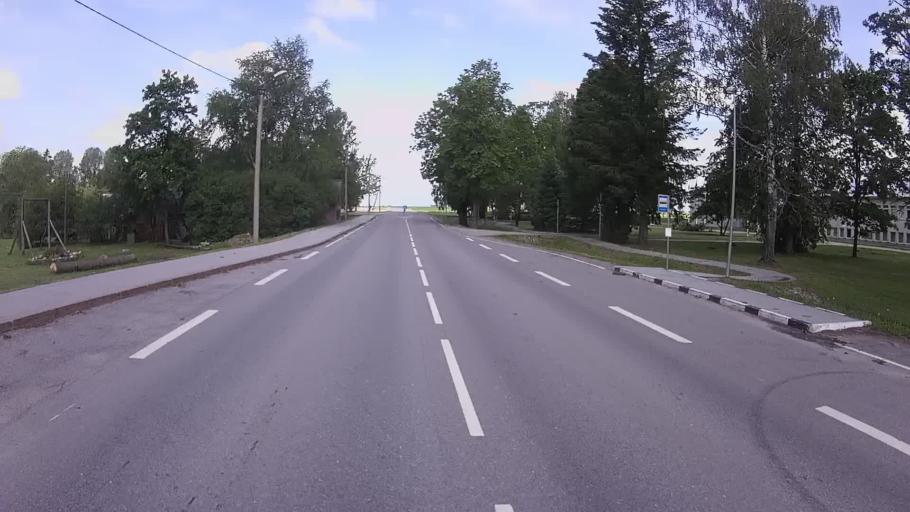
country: EE
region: Vorumaa
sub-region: Antsla vald
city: Vana-Antsla
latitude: 57.8925
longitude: 26.5012
